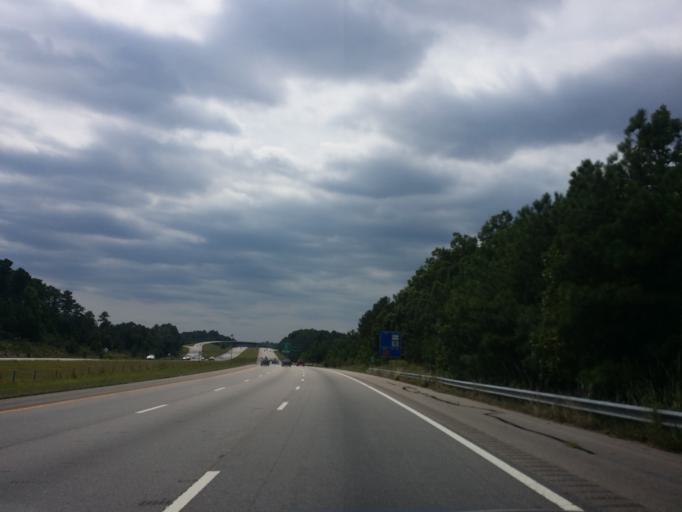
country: US
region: North Carolina
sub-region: Wake County
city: Morrisville
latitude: 35.9106
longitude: -78.7588
